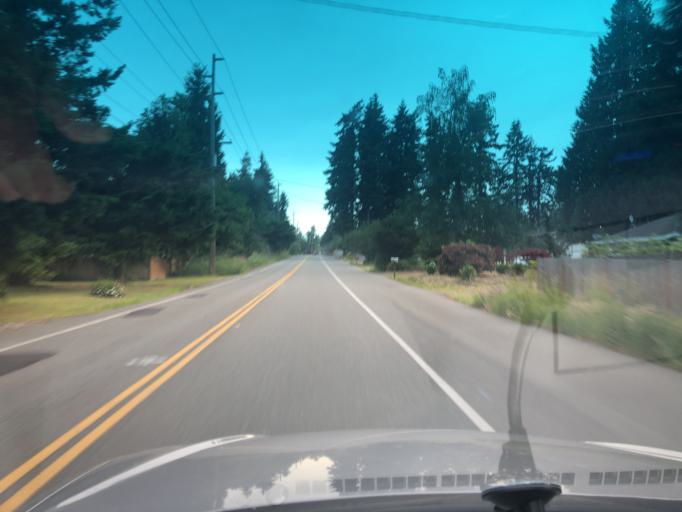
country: US
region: Washington
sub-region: King County
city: Lakeland North
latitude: 47.3390
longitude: -122.2708
